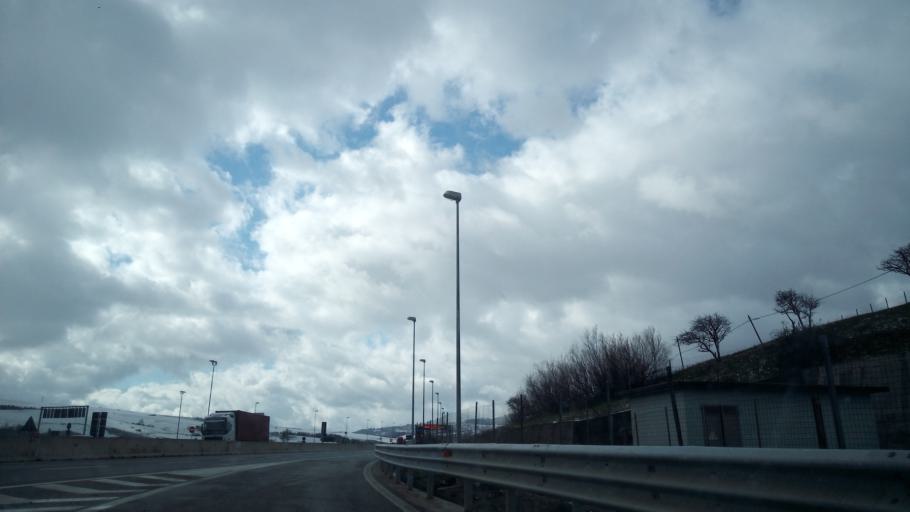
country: IT
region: Campania
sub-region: Provincia di Avellino
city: Scampitella
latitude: 41.0655
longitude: 15.3146
